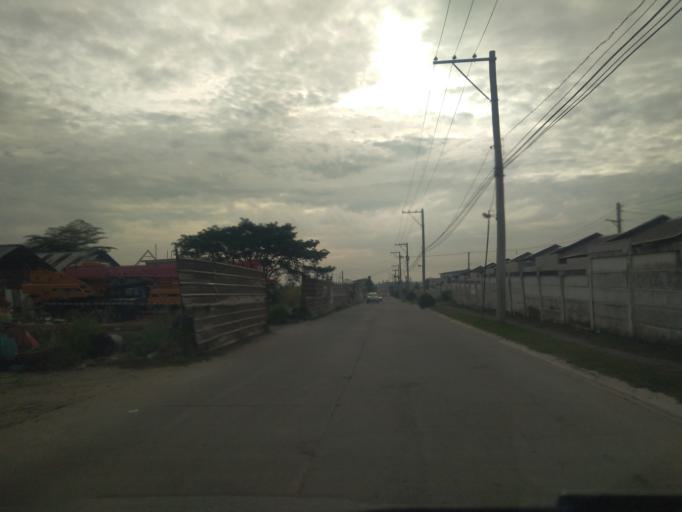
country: PH
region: Central Luzon
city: Santol
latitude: 15.1671
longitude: 120.5373
